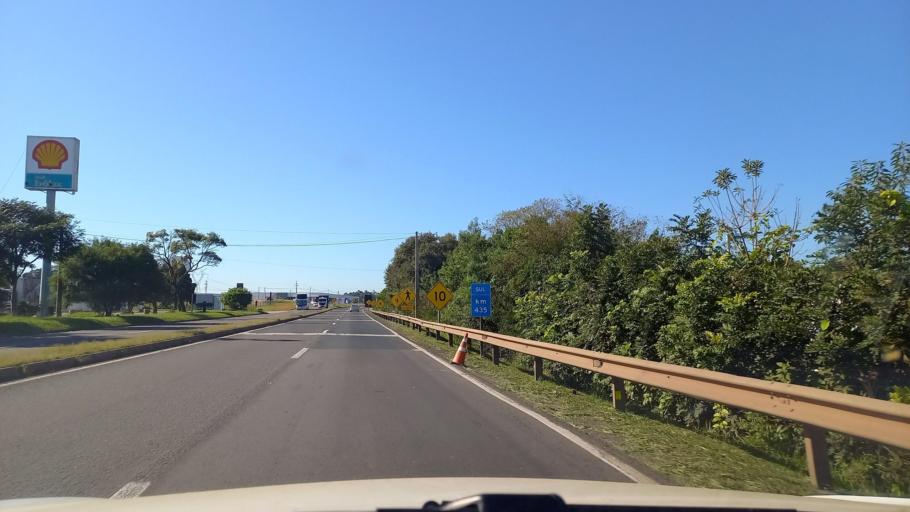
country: BR
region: Rio Grande do Sul
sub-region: Esteio
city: Esteio
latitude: -29.8469
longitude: -51.2745
